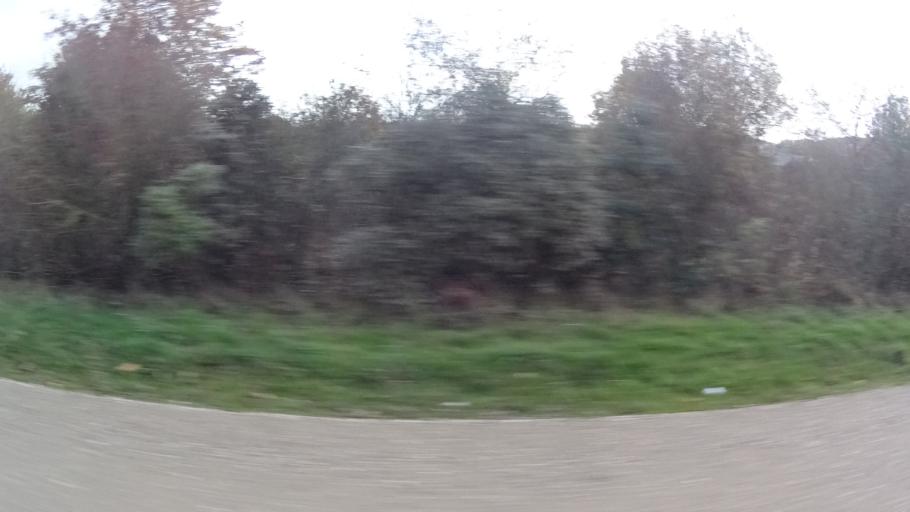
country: FR
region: Pays de la Loire
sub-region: Departement de la Loire-Atlantique
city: Saint-Nicolas-de-Redon
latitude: 47.6697
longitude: -2.0578
